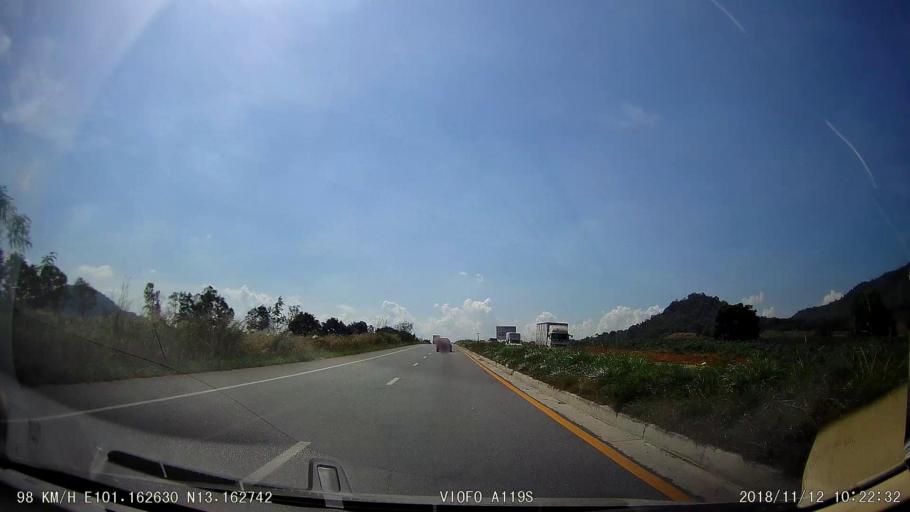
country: TH
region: Chon Buri
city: Ban Bueng
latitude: 13.1624
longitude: 101.1627
